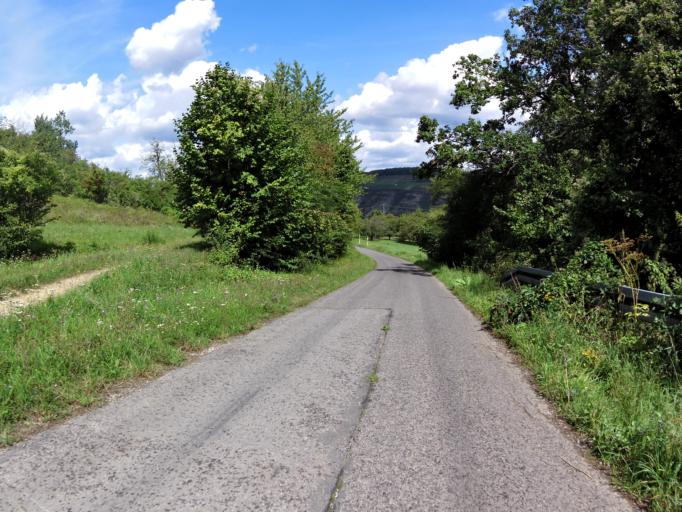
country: DE
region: Bavaria
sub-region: Regierungsbezirk Unterfranken
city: Margetshochheim
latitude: 49.8422
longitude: 9.8512
